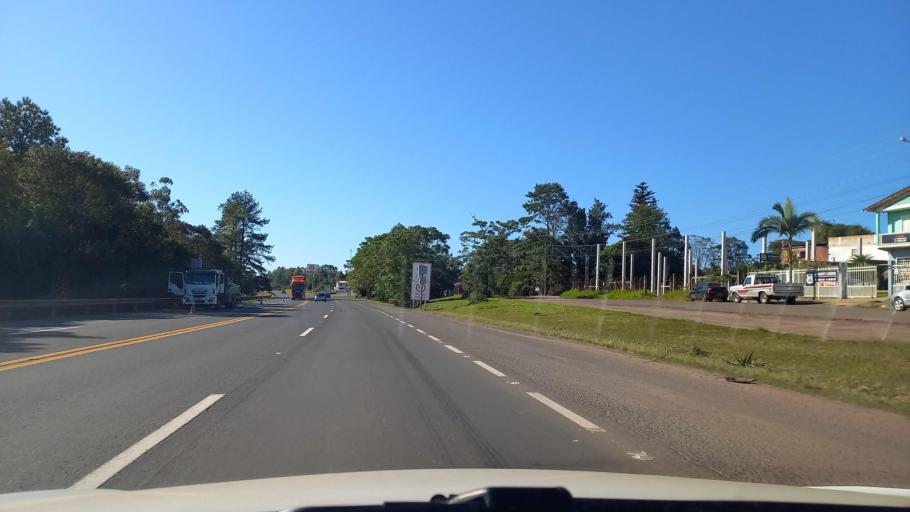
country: BR
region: Rio Grande do Sul
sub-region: Montenegro
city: Montenegro
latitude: -29.8179
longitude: -51.4717
